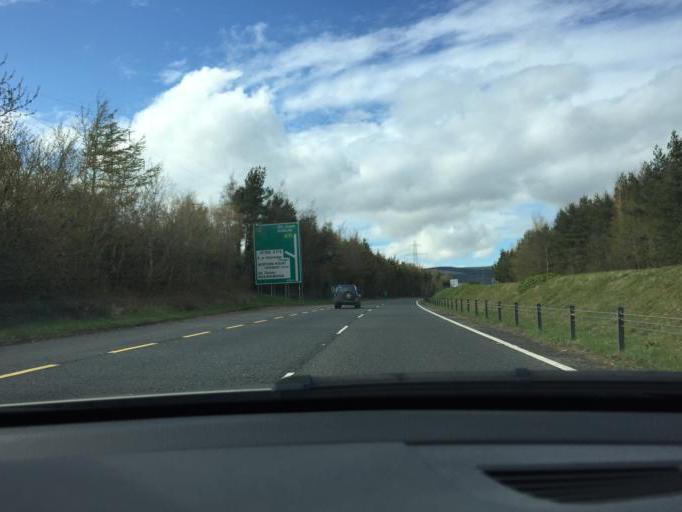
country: IE
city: Newtownmountkennedy
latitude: 53.0944
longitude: -6.1026
